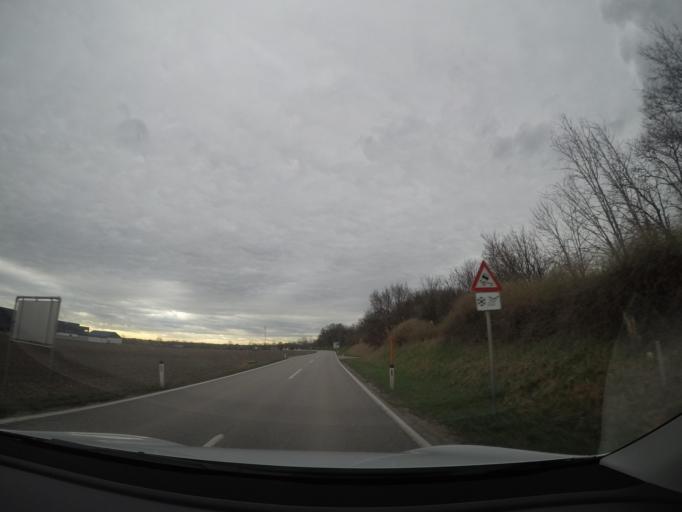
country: AT
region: Lower Austria
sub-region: Politischer Bezirk Modling
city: Biedermannsdorf
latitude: 48.0841
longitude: 16.3592
